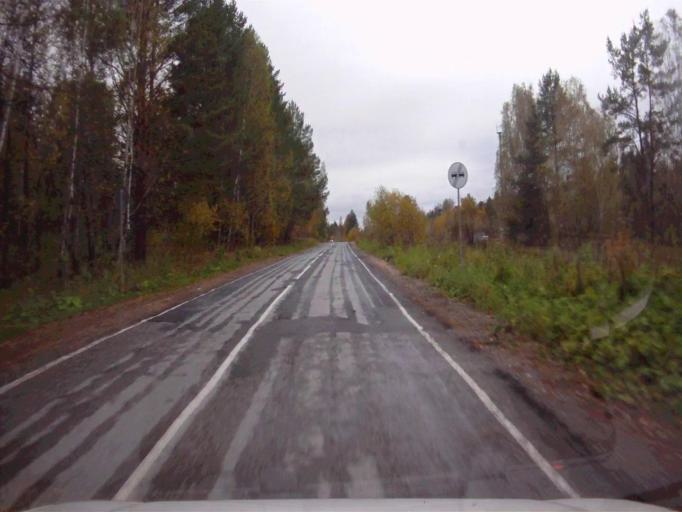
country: RU
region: Chelyabinsk
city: Nyazepetrovsk
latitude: 56.0505
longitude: 59.4881
